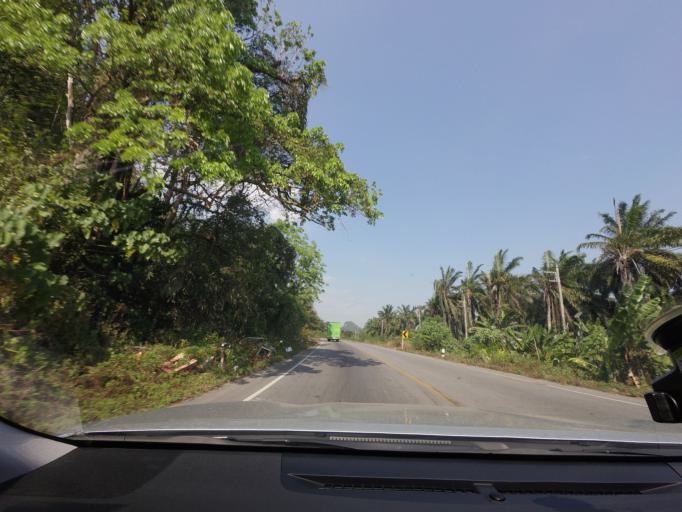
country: TH
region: Krabi
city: Plai Phraya
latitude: 8.5562
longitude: 98.7926
